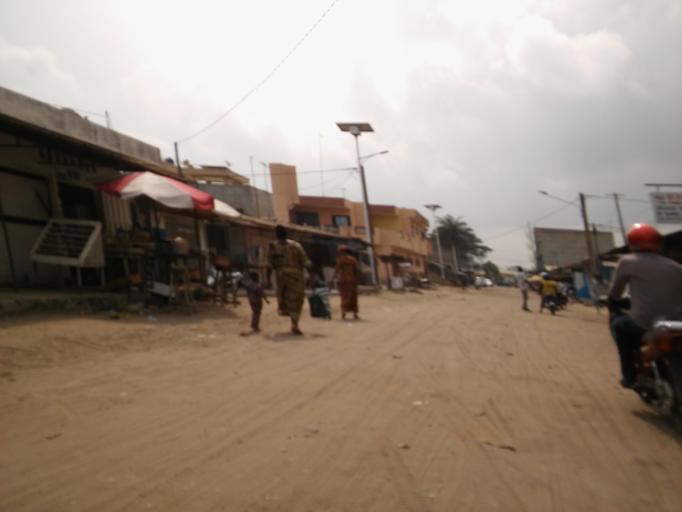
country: BJ
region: Littoral
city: Cotonou
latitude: 6.3897
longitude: 2.3850
